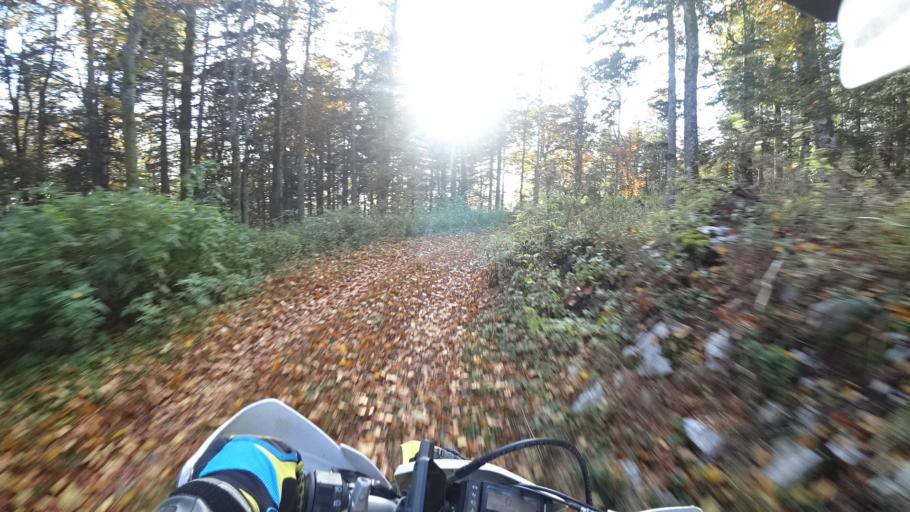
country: HR
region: Karlovacka
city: Plaski
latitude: 44.9507
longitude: 15.4058
